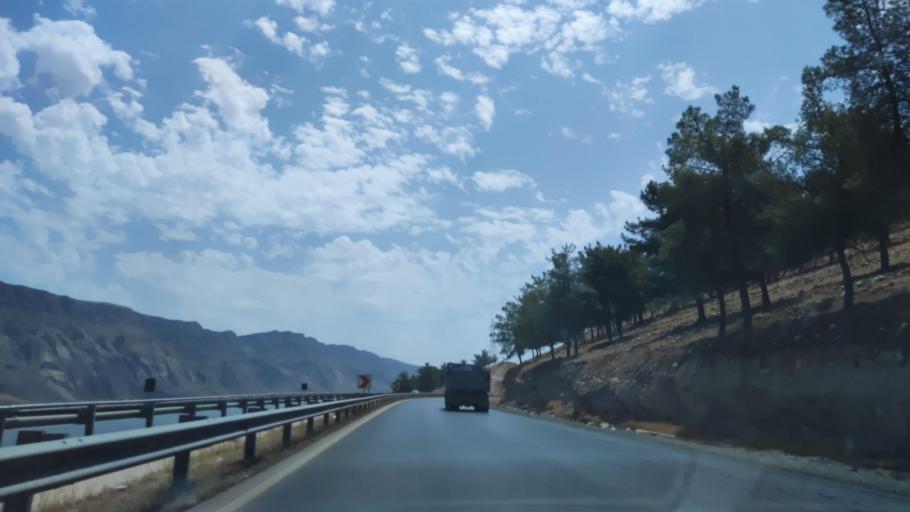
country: IQ
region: Arbil
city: Shaqlawah
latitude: 36.4900
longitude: 44.3773
